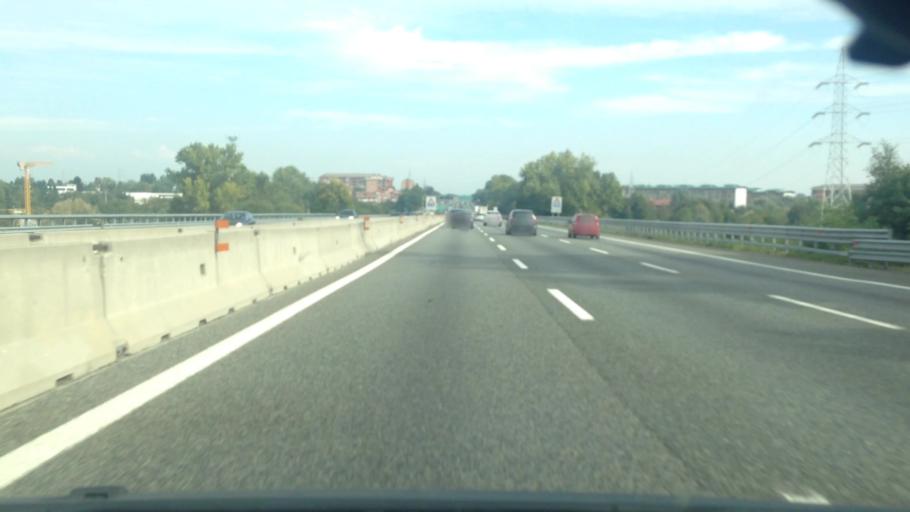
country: IT
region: Piedmont
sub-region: Provincia di Torino
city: Collegno
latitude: 45.0864
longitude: 7.5605
